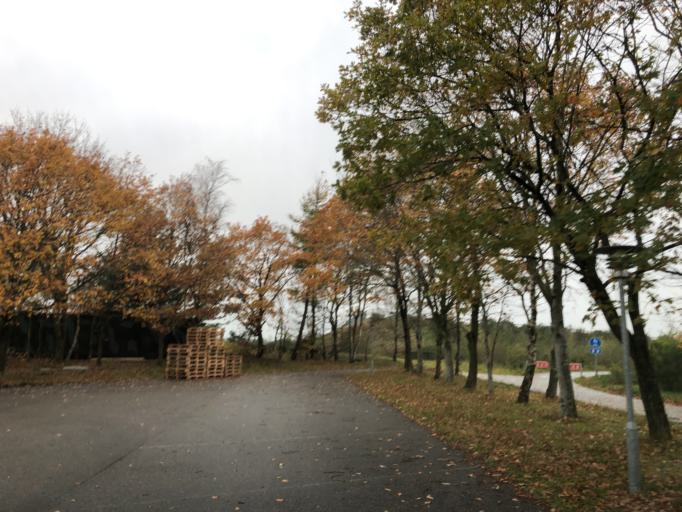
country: DK
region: Central Jutland
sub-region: Herning Kommune
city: Sunds
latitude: 56.2057
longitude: 8.9921
